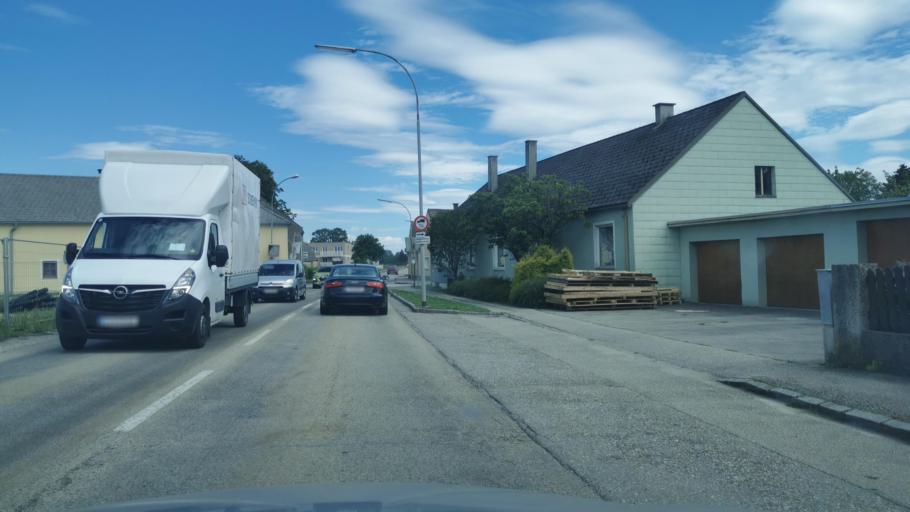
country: AT
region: Lower Austria
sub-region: Sankt Polten Stadt
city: Sankt Poelten
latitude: 48.1740
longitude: 15.6245
